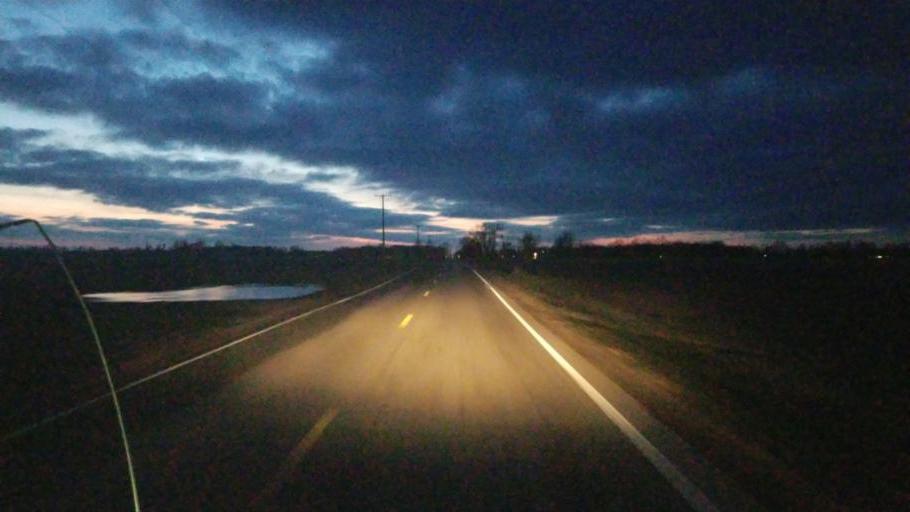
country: US
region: Ohio
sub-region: Union County
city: Richwood
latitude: 40.4593
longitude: -83.2925
